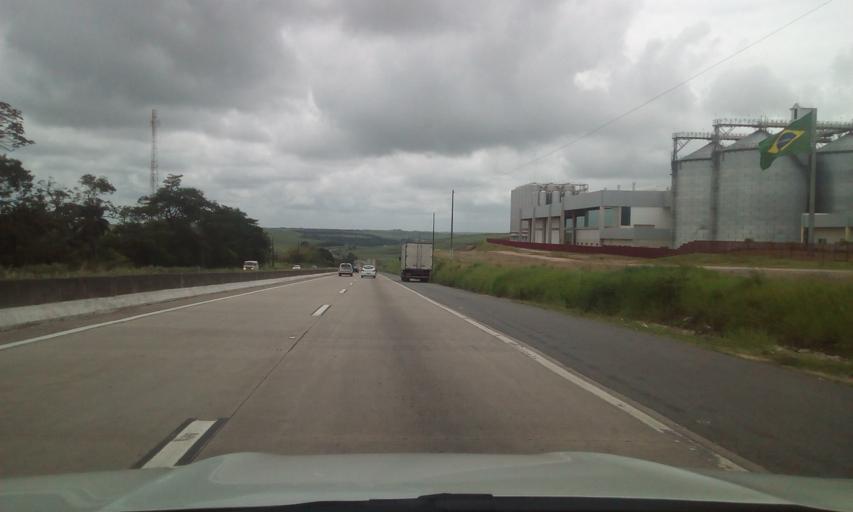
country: BR
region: Pernambuco
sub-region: Itapissuma
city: Itapissuma
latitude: -7.7909
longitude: -34.9291
